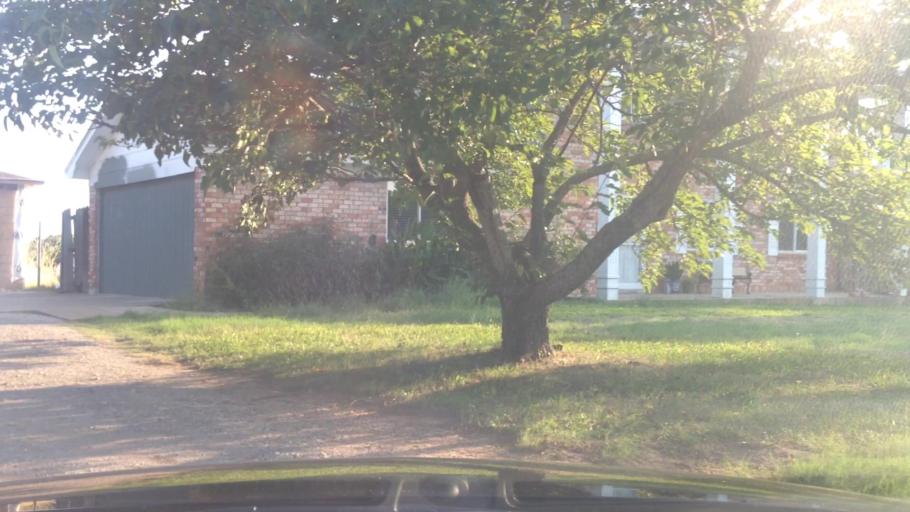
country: US
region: Texas
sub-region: Tarrant County
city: Rendon
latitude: 32.5906
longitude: -97.2594
